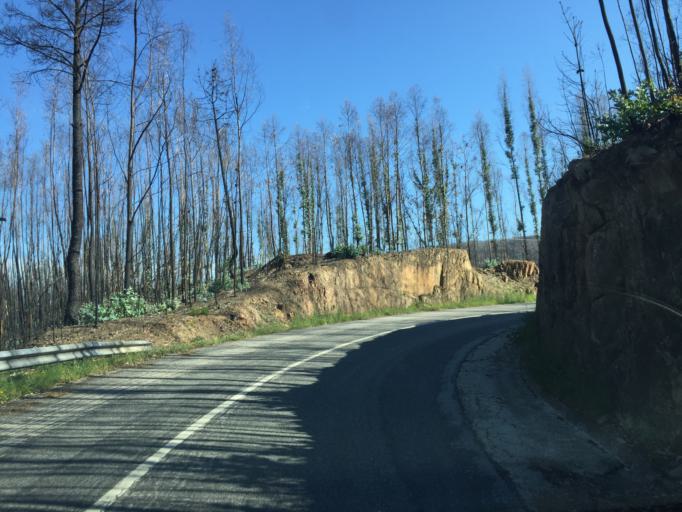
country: PT
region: Coimbra
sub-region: Pampilhosa da Serra
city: Pampilhosa da Serra
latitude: 40.0394
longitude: -7.9247
